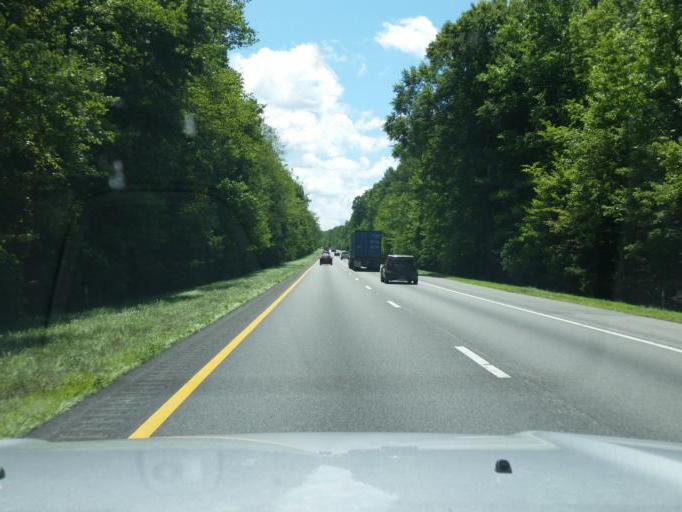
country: US
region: Virginia
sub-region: King William County
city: West Point
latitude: 37.4335
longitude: -76.8459
